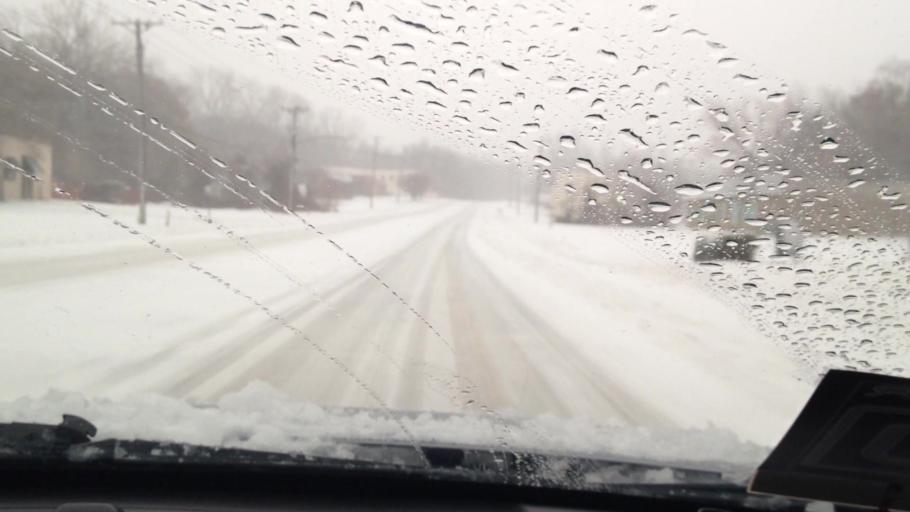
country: US
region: Missouri
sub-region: Jackson County
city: Raytown
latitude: 39.0222
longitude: -94.4675
